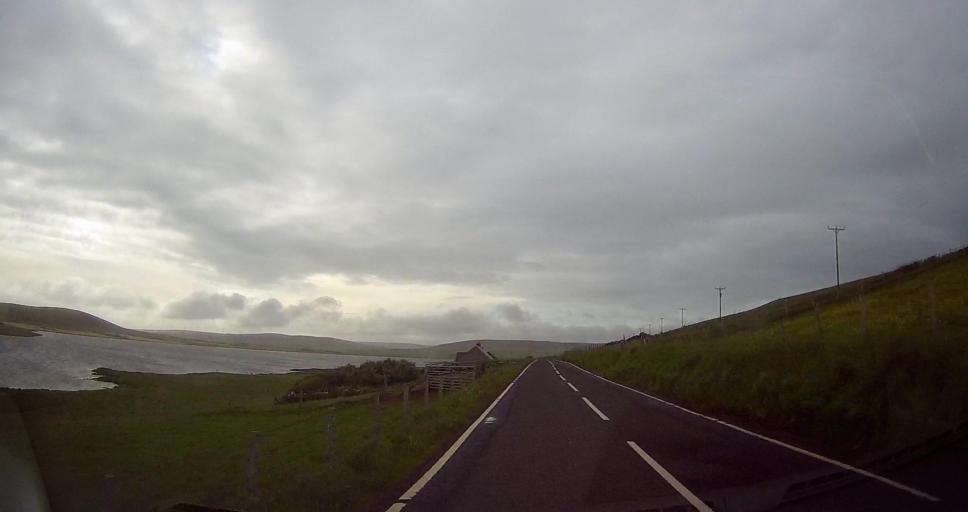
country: GB
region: Scotland
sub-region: Orkney Islands
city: Stromness
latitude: 59.1128
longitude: -3.2970
